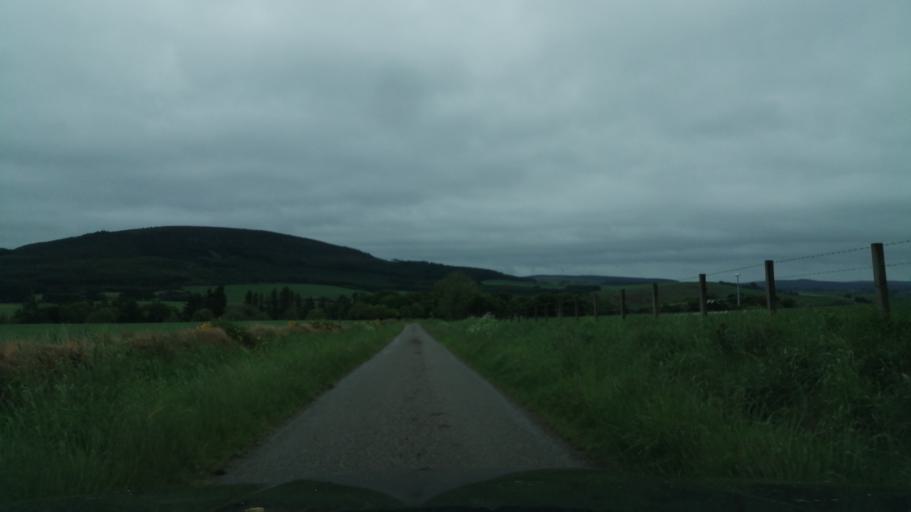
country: GB
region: Scotland
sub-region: Moray
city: Keith
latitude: 57.5554
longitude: -2.8681
